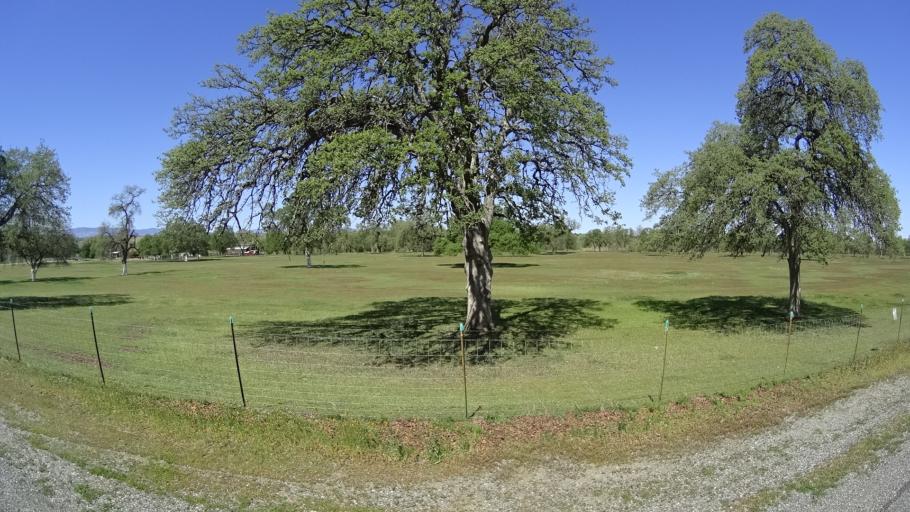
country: US
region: California
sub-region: Glenn County
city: Orland
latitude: 39.7331
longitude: -122.4017
